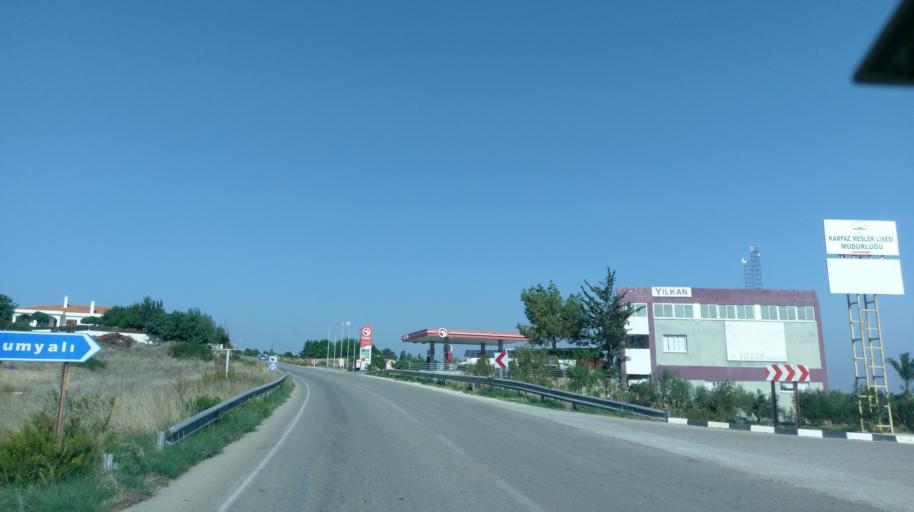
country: CY
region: Ammochostos
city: Leonarisso
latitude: 35.4207
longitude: 34.1254
